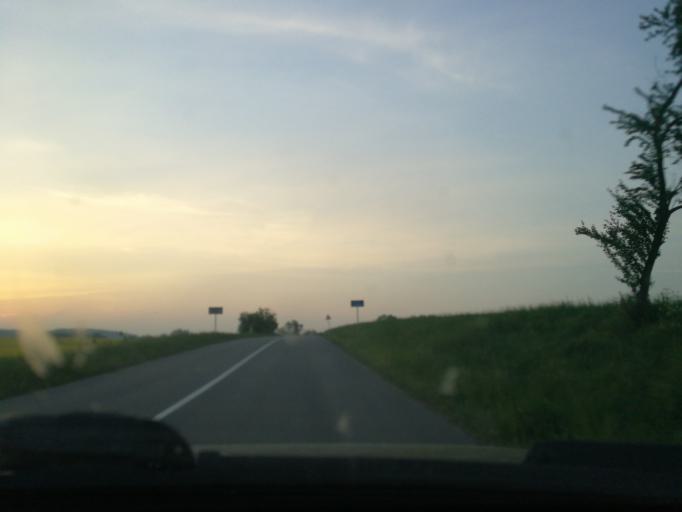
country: CZ
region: Zlin
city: Tecovice
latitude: 49.2602
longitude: 17.5597
